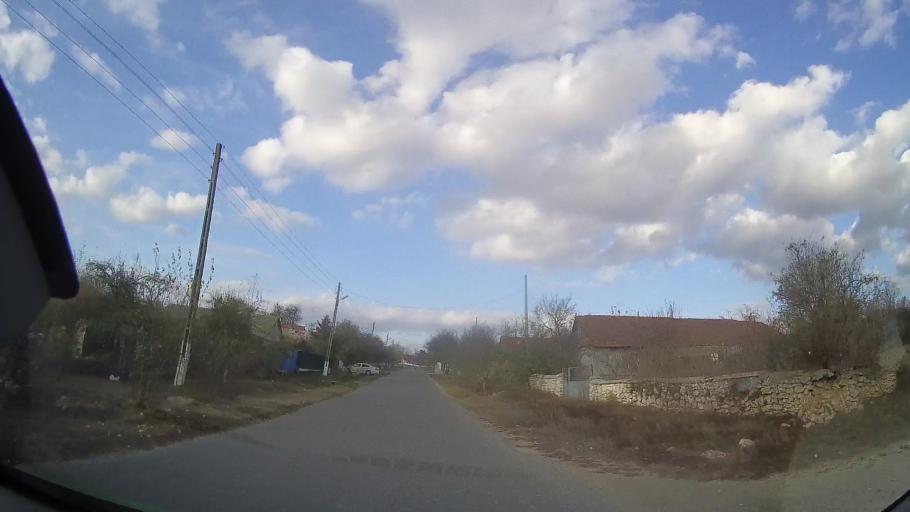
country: RO
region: Constanta
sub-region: Comuna Cerchezu
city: Cerchezu
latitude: 43.8588
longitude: 28.1013
